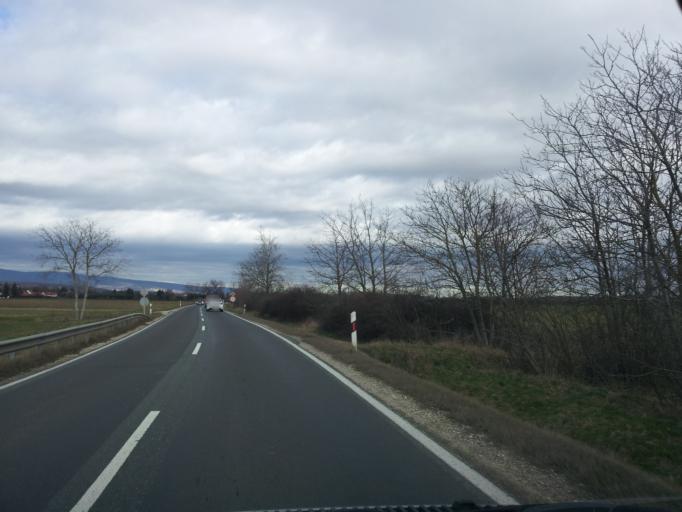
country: HU
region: Vas
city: Gencsapati
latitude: 47.3098
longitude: 16.5947
